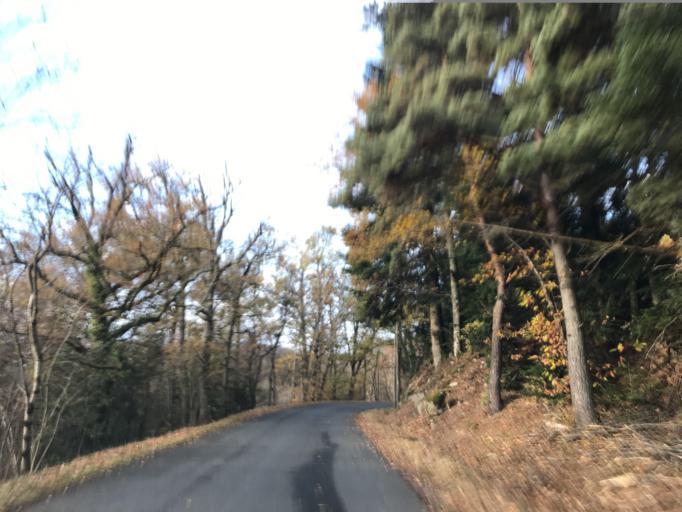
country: FR
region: Auvergne
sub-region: Departement du Puy-de-Dome
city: Celles-sur-Durolle
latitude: 45.7723
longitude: 3.6457
